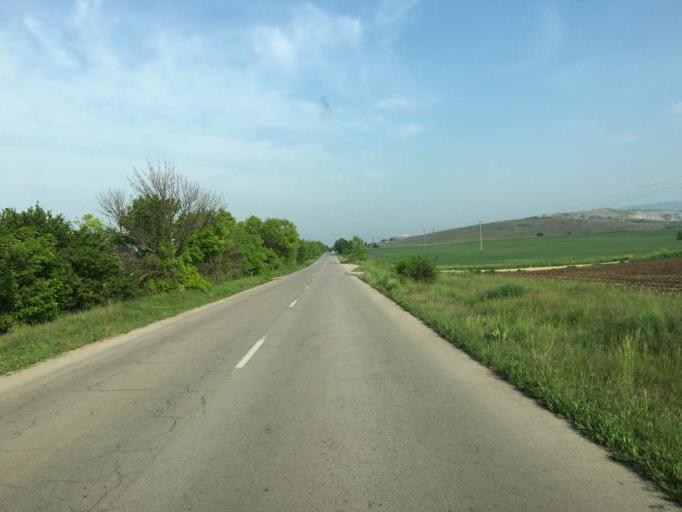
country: BG
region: Pernik
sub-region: Obshtina Radomir
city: Radomir
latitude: 42.4913
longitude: 23.0431
